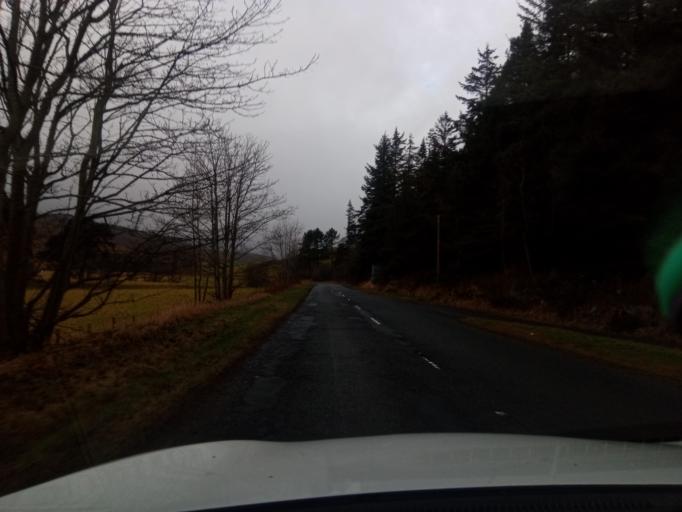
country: GB
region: Scotland
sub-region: The Scottish Borders
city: Peebles
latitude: 55.6515
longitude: -3.2730
